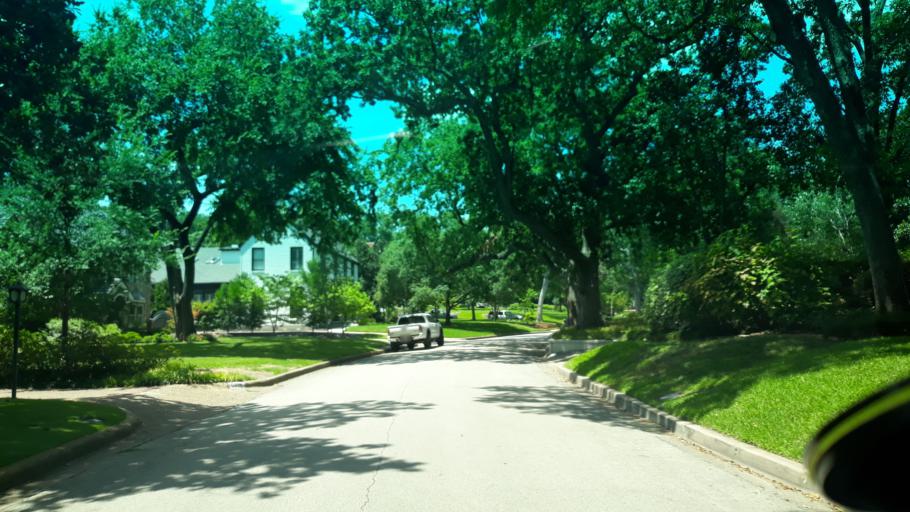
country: US
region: Texas
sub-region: Dallas County
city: Highland Park
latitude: 32.8191
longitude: -96.7396
